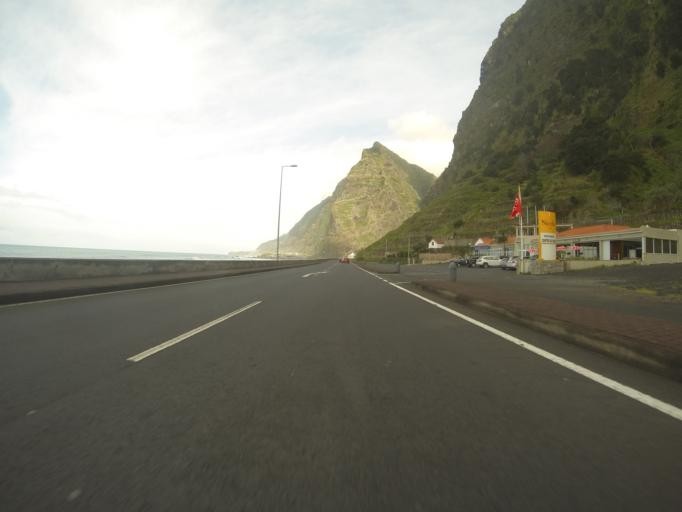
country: PT
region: Madeira
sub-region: Sao Vicente
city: Sao Vicente
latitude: 32.8091
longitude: -17.0580
